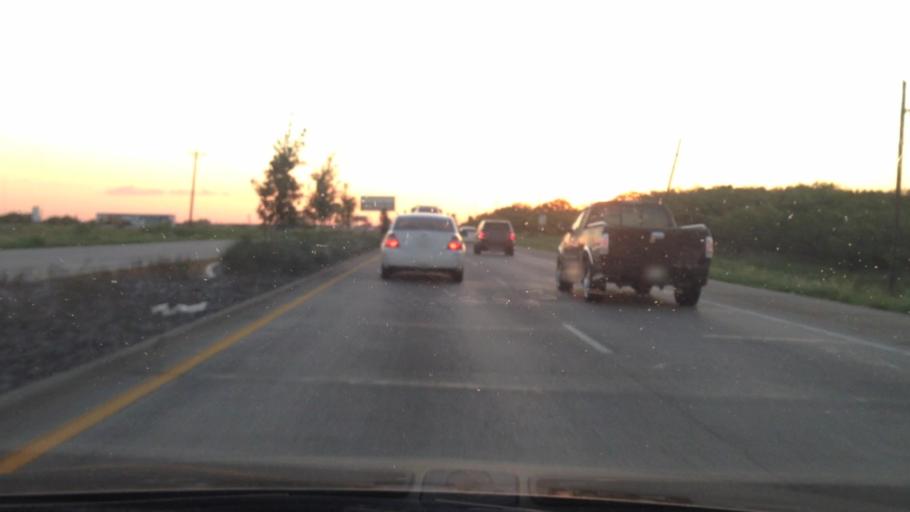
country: US
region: Texas
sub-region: Denton County
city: The Colony
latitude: 33.0498
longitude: -96.9285
